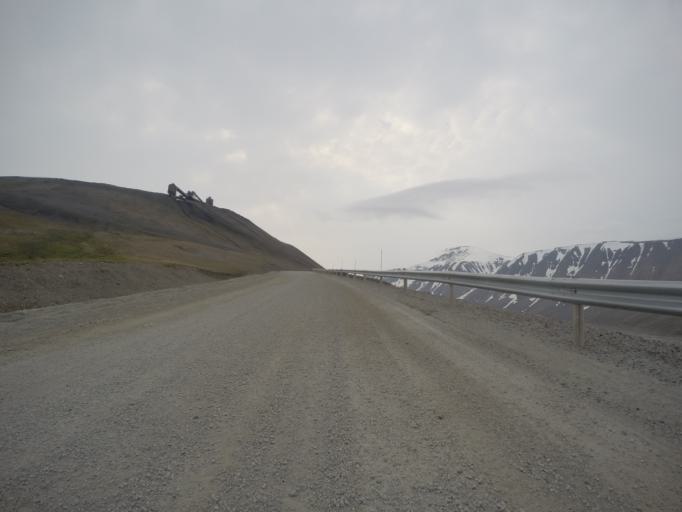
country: SJ
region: Svalbard
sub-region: Spitsbergen
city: Longyearbyen
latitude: 78.1616
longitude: 16.0330
